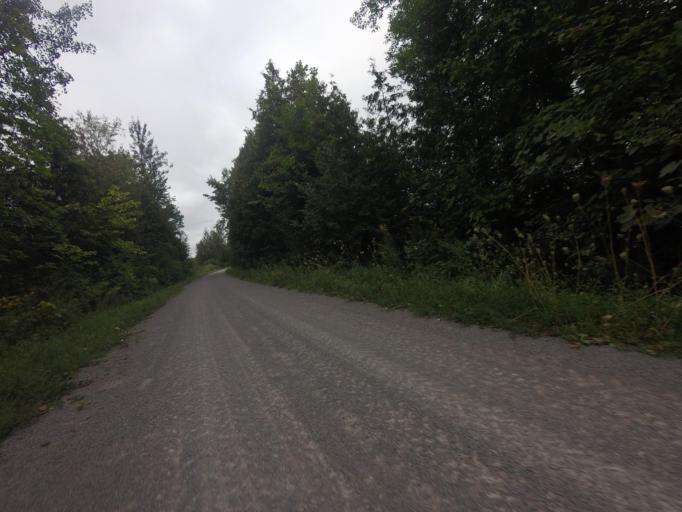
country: CA
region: Ontario
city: Omemee
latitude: 44.4178
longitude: -78.7783
